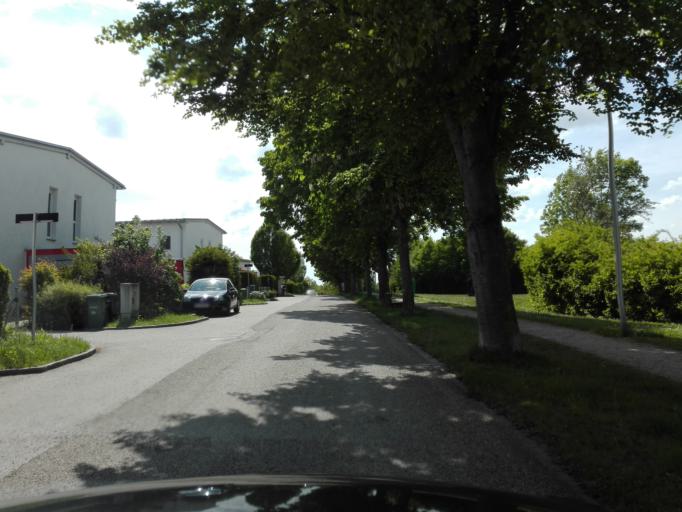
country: AT
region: Upper Austria
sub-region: Politischer Bezirk Linz-Land
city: Leonding
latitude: 48.2706
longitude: 14.2594
